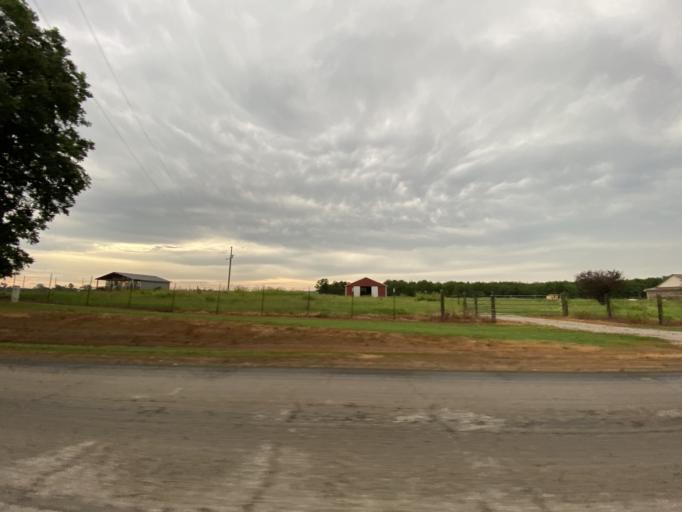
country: US
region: Alabama
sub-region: Lawrence County
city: Moulton
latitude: 34.4641
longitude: -87.5001
